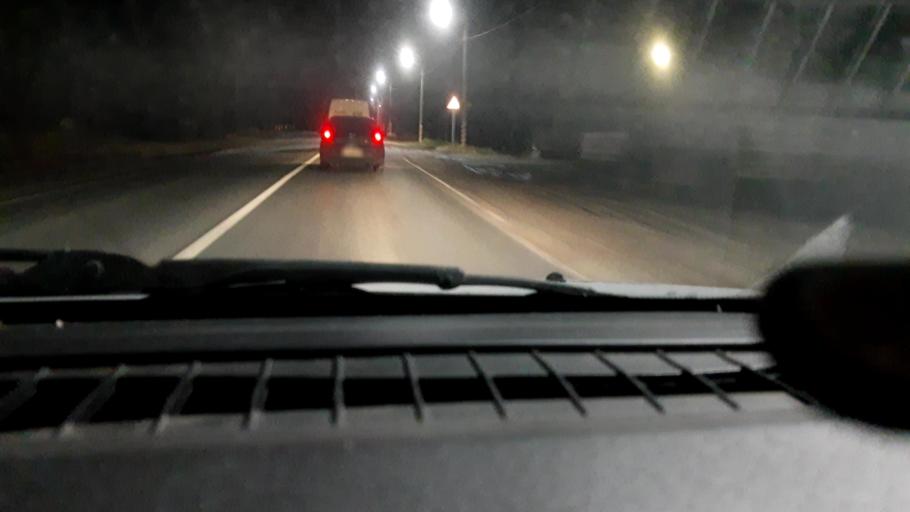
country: RU
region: Nizjnij Novgorod
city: Linda
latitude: 56.5697
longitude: 44.0244
